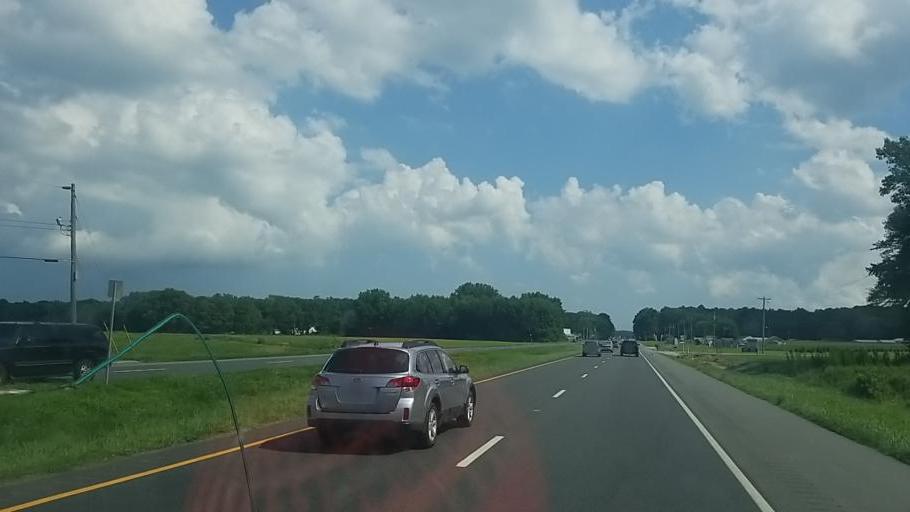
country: US
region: Delaware
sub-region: Sussex County
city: Millsboro
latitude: 38.5346
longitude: -75.2523
